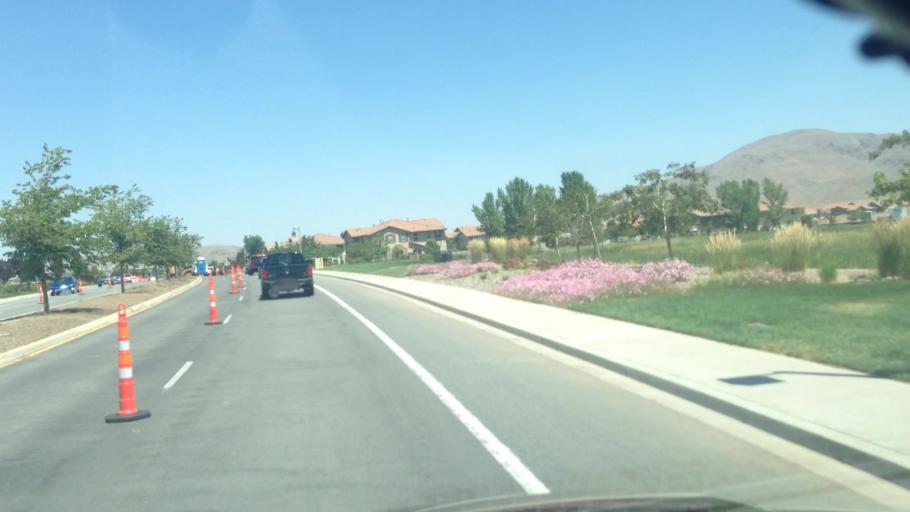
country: US
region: Nevada
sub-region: Washoe County
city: Sparks
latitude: 39.4197
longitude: -119.7325
